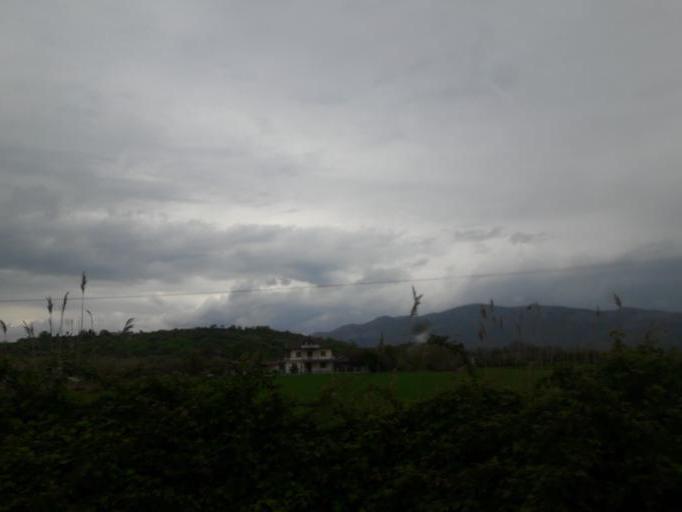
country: AL
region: Shkoder
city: Vukatane
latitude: 42.0064
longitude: 19.5356
